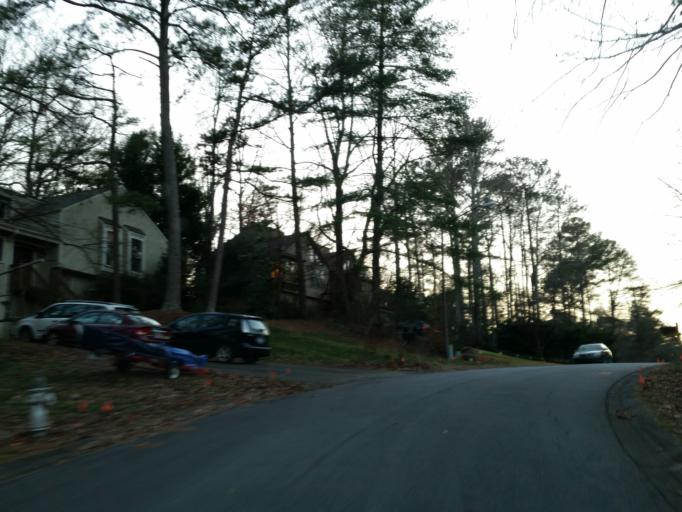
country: US
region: Georgia
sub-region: Fulton County
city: Sandy Springs
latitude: 33.9602
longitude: -84.3994
